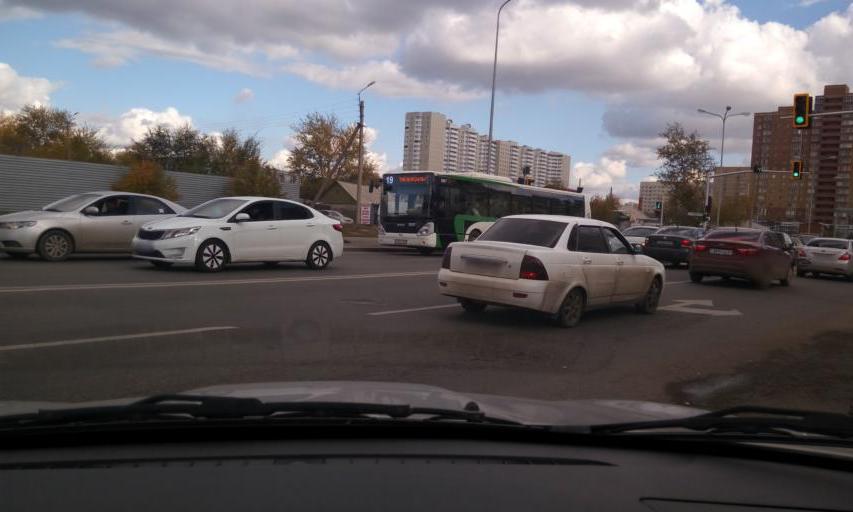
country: KZ
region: Astana Qalasy
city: Astana
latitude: 51.1630
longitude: 71.4523
